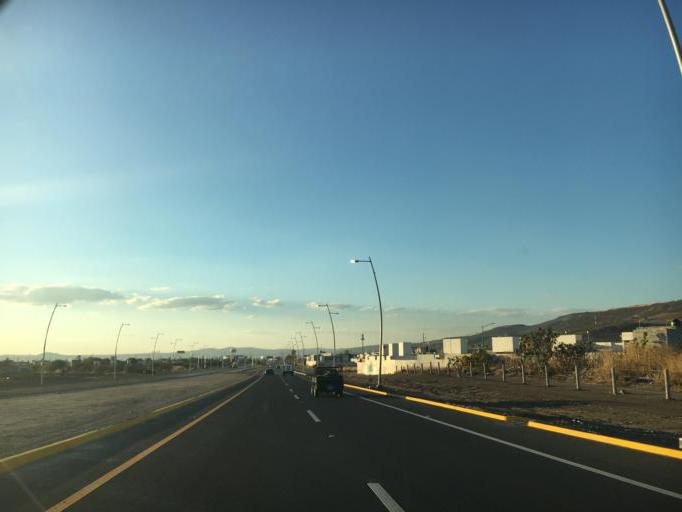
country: MX
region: Guanajuato
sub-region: Leon
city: Fraccionamiento Paraiso Real
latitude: 21.1011
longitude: -101.5744
